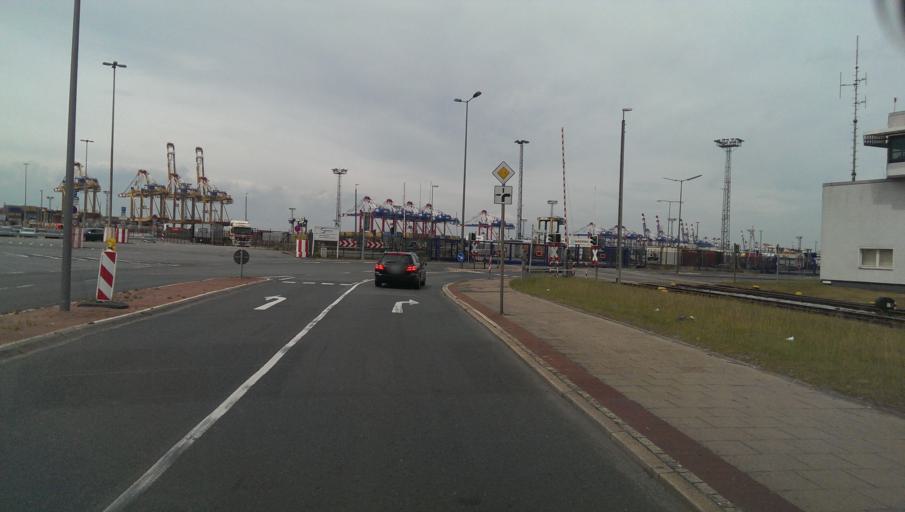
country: DE
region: Bremen
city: Bremerhaven
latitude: 53.5812
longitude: 8.5474
